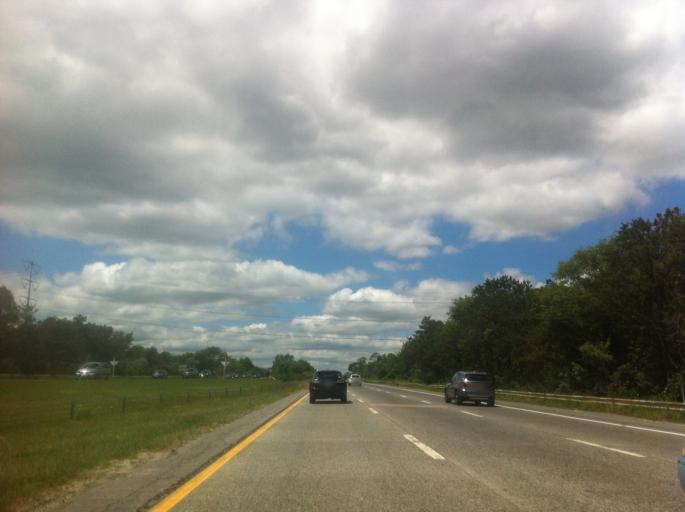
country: US
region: New York
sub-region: Suffolk County
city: Yaphank
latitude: 40.8294
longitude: -72.9360
